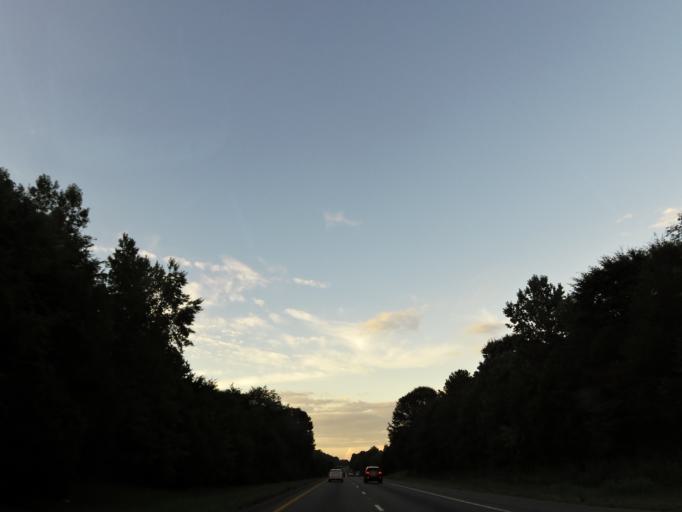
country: US
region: Tennessee
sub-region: McMinn County
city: Athens
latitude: 35.4414
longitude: -84.6736
